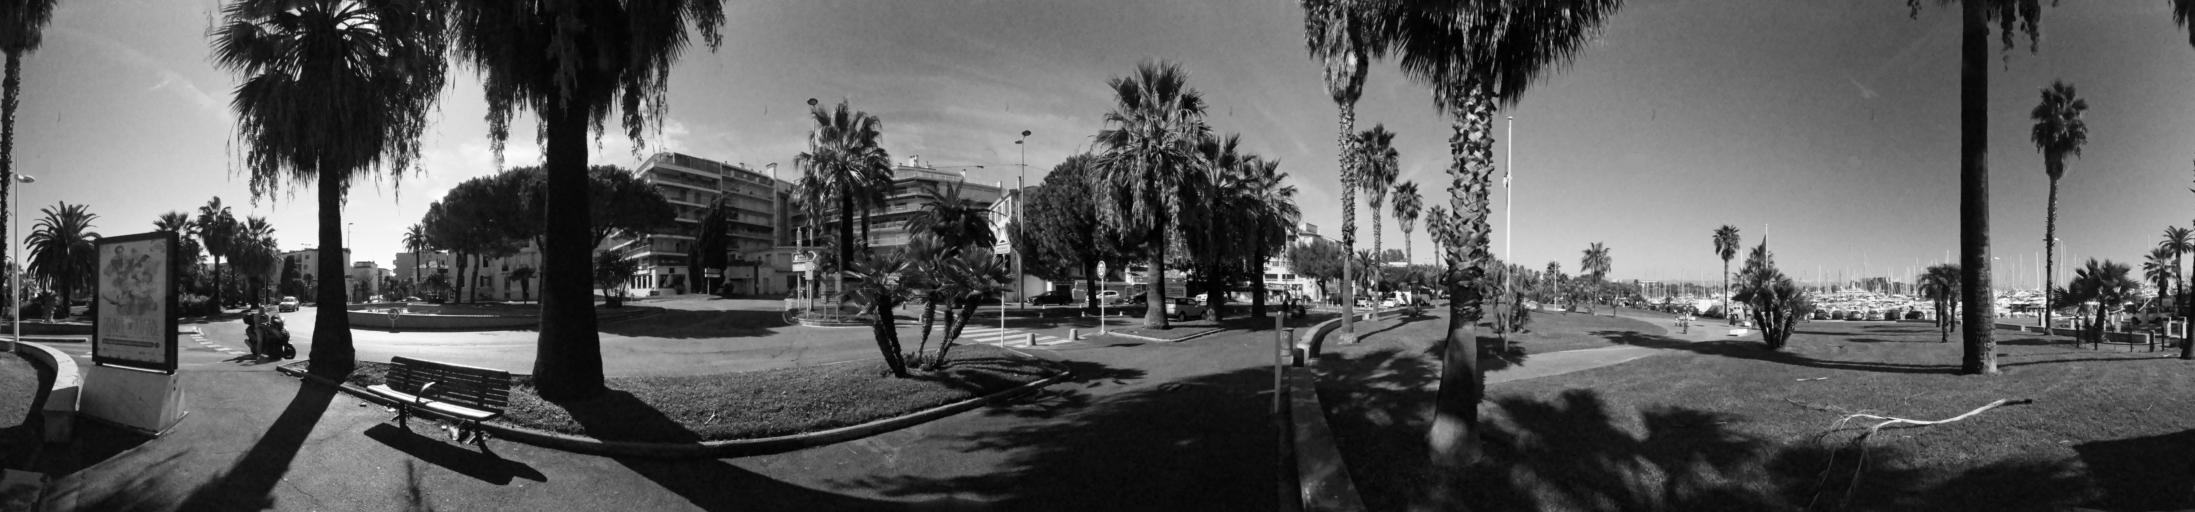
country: FR
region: Provence-Alpes-Cote d'Azur
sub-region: Departement des Alpes-Maritimes
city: Antibes
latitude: 43.5846
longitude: 7.1219
